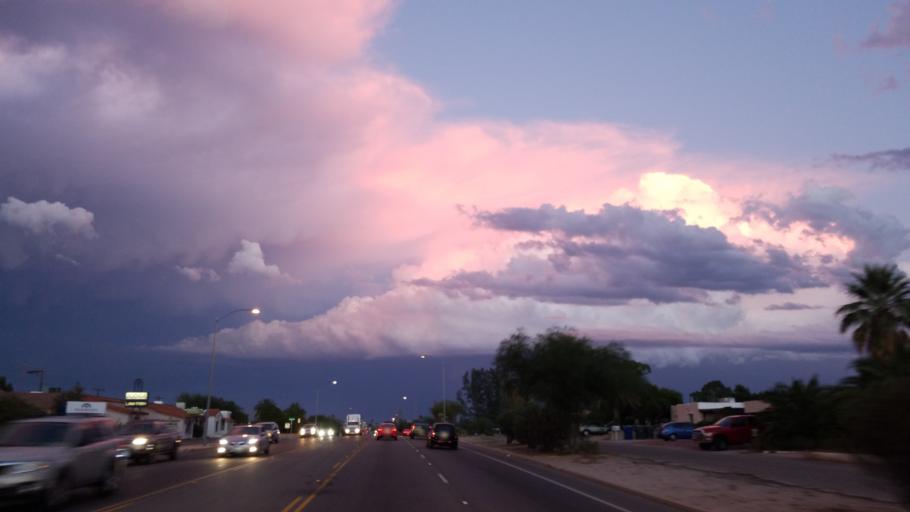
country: US
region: Arizona
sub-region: Pima County
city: Tucson
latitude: 32.2502
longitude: -110.9411
